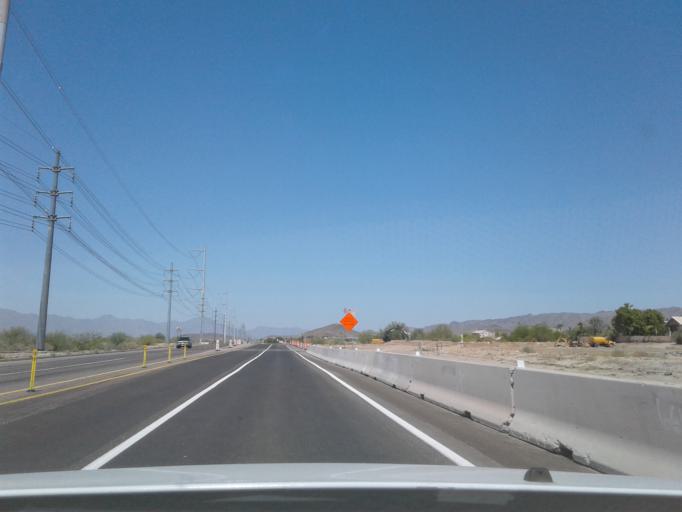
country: US
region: Arizona
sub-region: Maricopa County
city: Guadalupe
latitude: 33.2911
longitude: -112.0202
